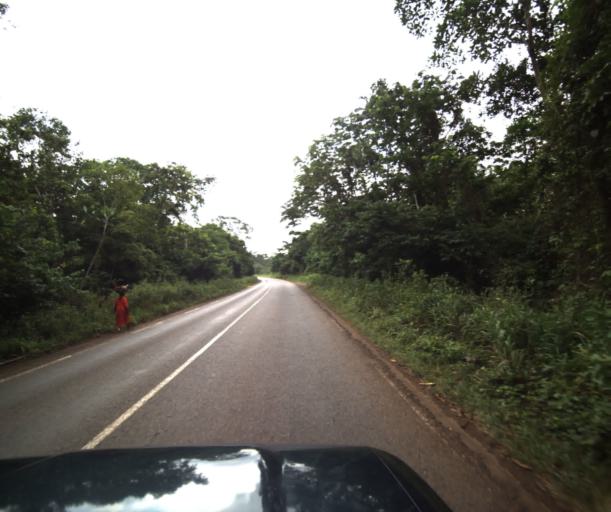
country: CM
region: Centre
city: Eseka
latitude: 3.8929
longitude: 10.7234
